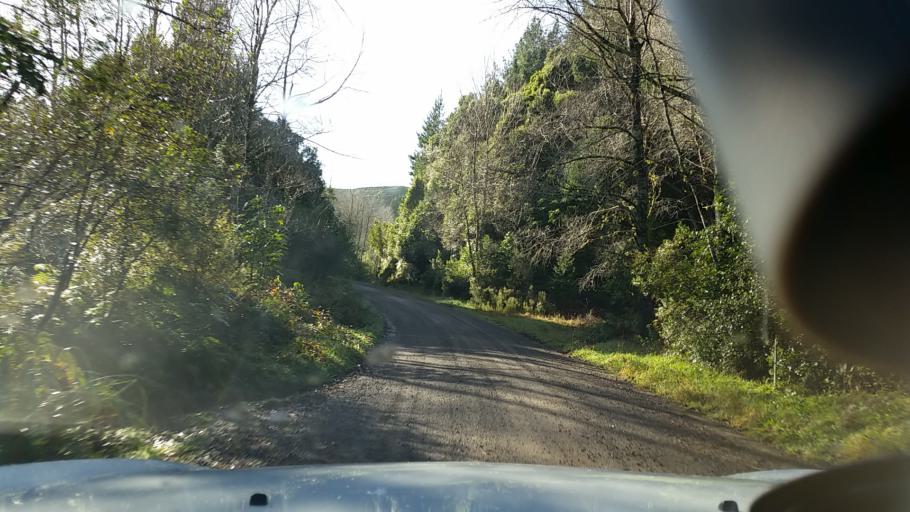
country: NZ
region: Bay of Plenty
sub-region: Kawerau District
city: Kawerau
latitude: -38.0027
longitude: 176.5977
